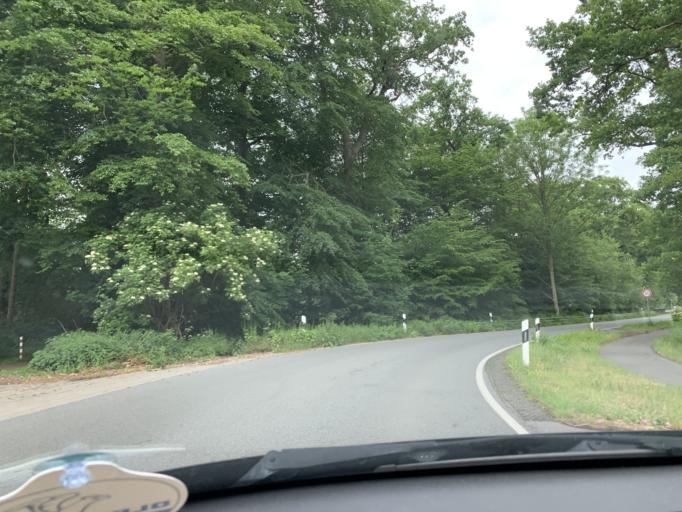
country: DE
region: Lower Saxony
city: Varel
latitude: 53.3769
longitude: 8.0808
